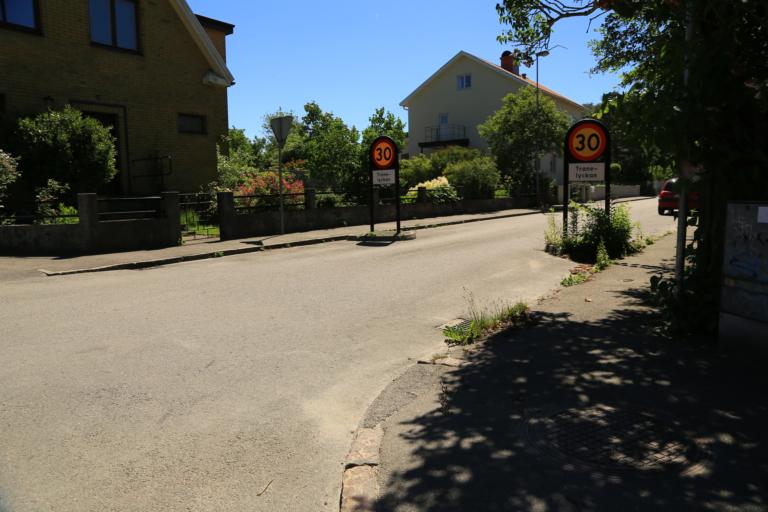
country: SE
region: Halland
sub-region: Varbergs Kommun
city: Varberg
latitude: 57.1031
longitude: 12.2617
